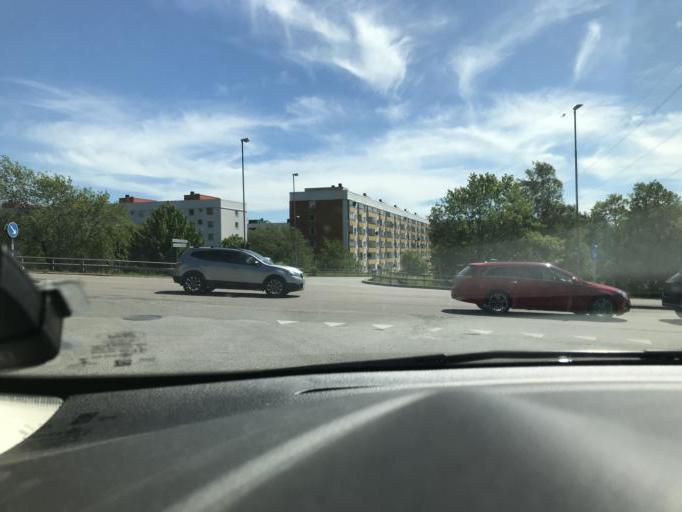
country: SE
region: Stockholm
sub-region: Botkyrka Kommun
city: Alby
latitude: 59.2392
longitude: 17.8383
